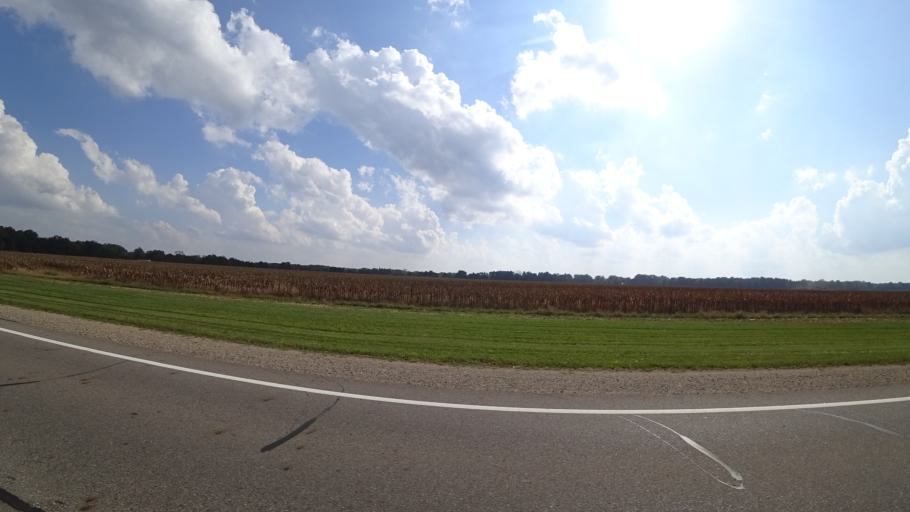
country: US
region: Michigan
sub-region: Saint Joseph County
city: Three Rivers
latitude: 41.9548
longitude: -85.5965
